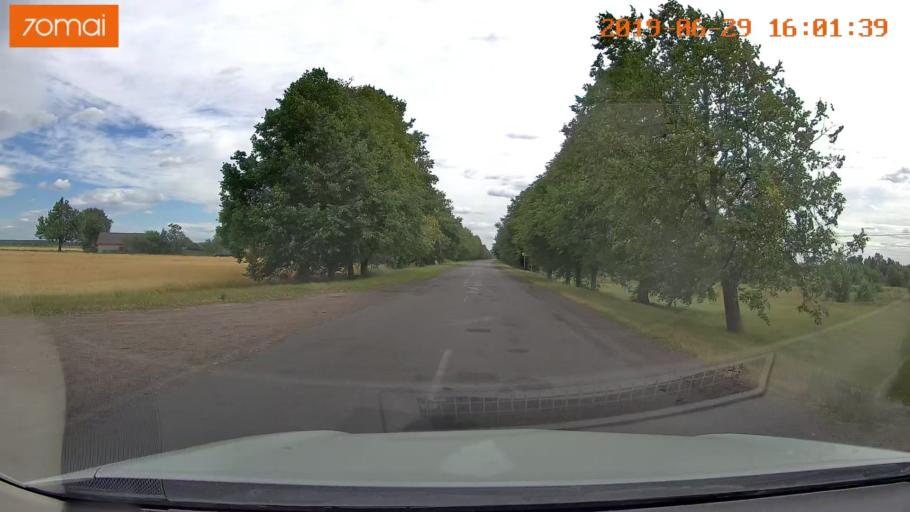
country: BY
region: Brest
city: Luninyets
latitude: 52.2445
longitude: 27.0164
